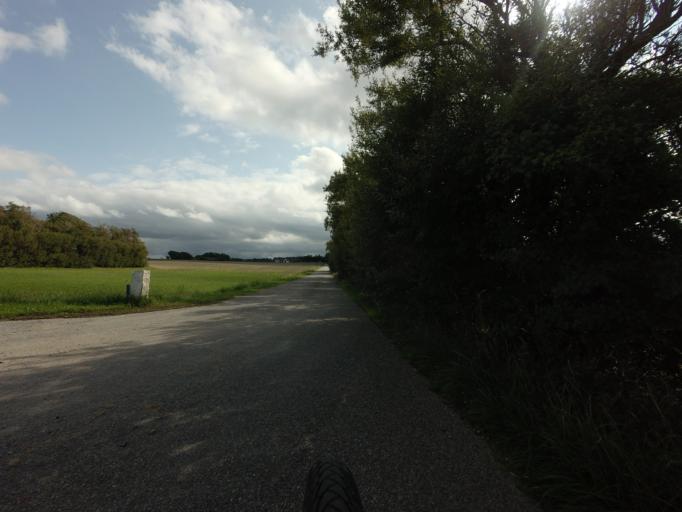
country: DK
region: North Denmark
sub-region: Hjorring Kommune
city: Hjorring
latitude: 57.5233
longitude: 10.0467
